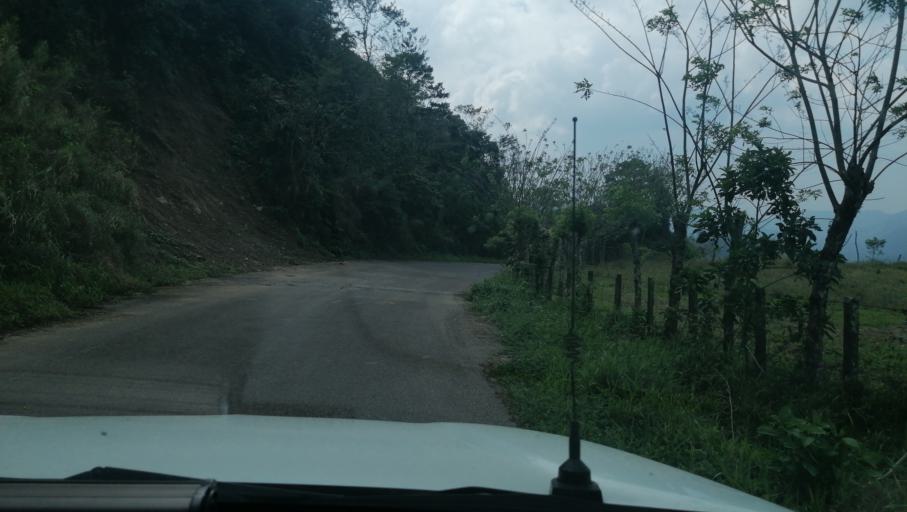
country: MX
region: Chiapas
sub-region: Francisco Leon
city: San Miguel la Sardina
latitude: 17.2373
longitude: -93.3225
